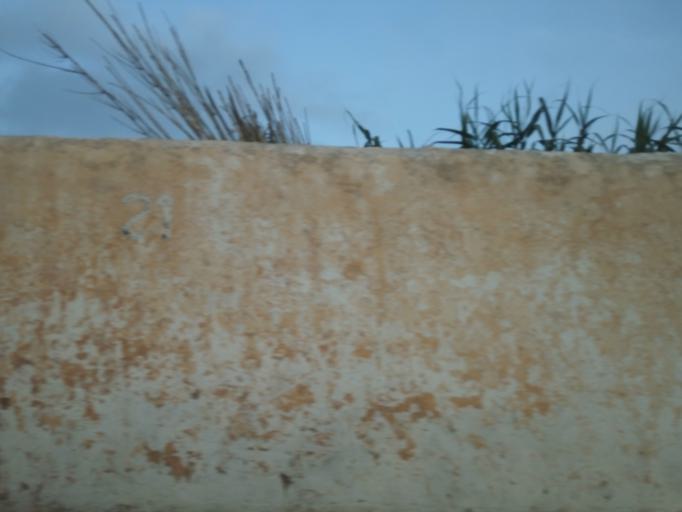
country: DZ
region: Tipaza
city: Bou Ismail
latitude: 36.6091
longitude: 2.6248
